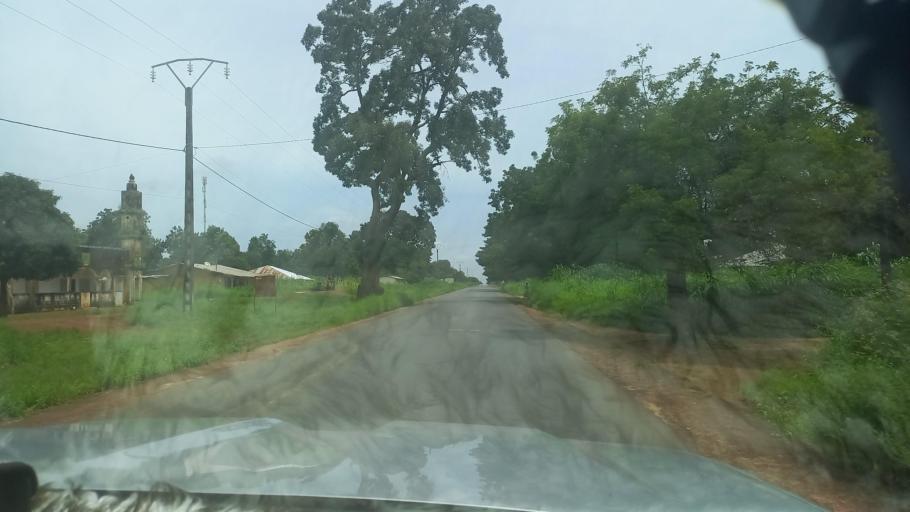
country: SN
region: Kolda
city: Marsassoum
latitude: 12.9617
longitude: -15.9869
